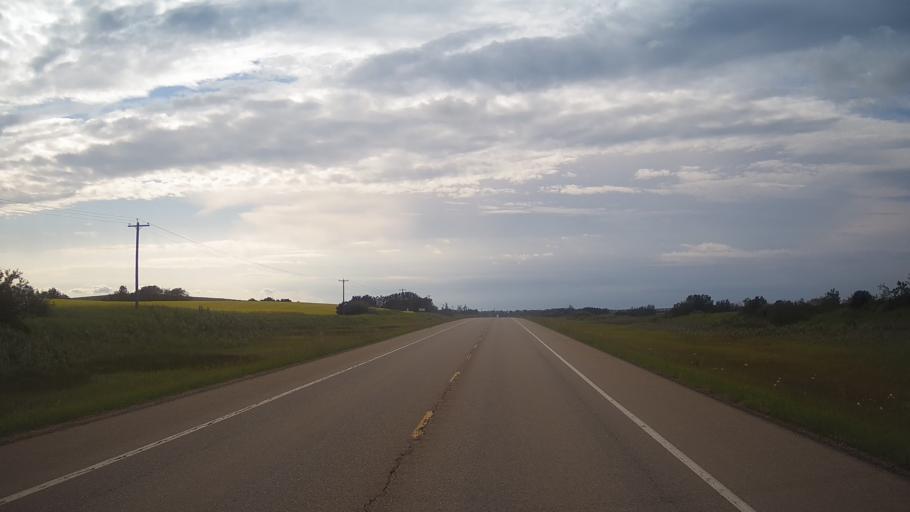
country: CA
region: Alberta
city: Viking
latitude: 53.0769
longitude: -111.7309
